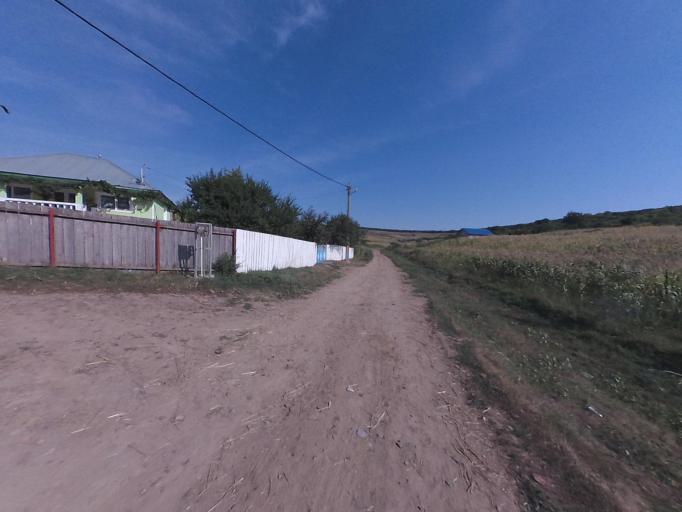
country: RO
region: Vaslui
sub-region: Comuna Osesti
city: Buda
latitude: 46.7687
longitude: 27.4304
